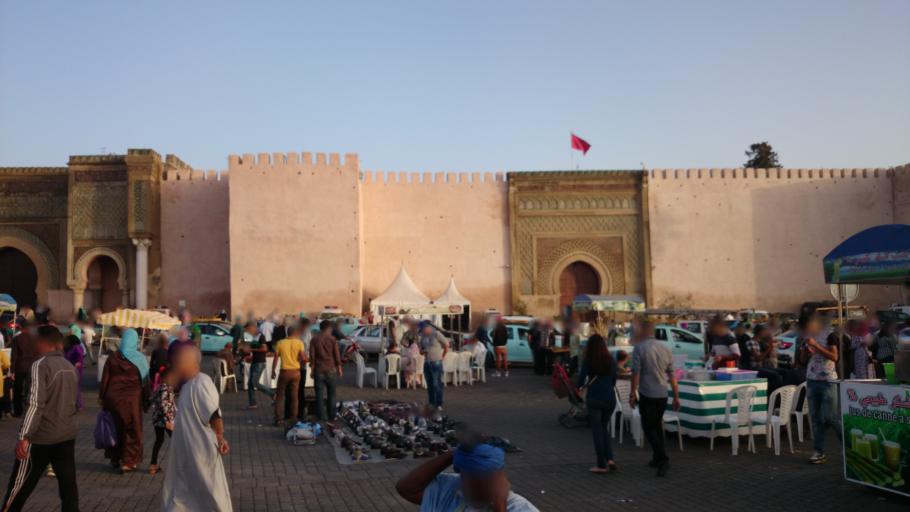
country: MA
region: Meknes-Tafilalet
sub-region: Meknes
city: Meknes
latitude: 33.8931
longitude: -5.5655
